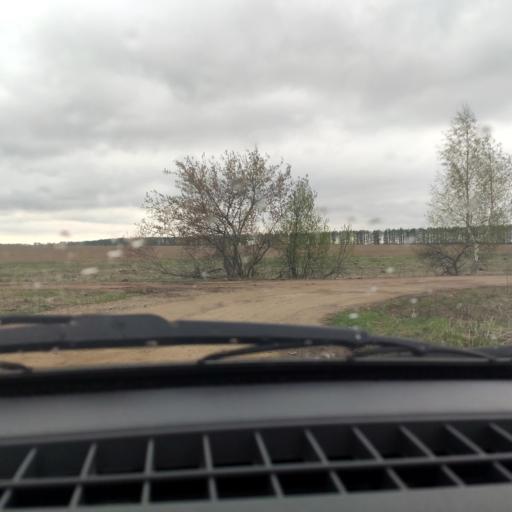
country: RU
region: Bashkortostan
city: Iglino
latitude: 54.7485
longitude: 56.2600
